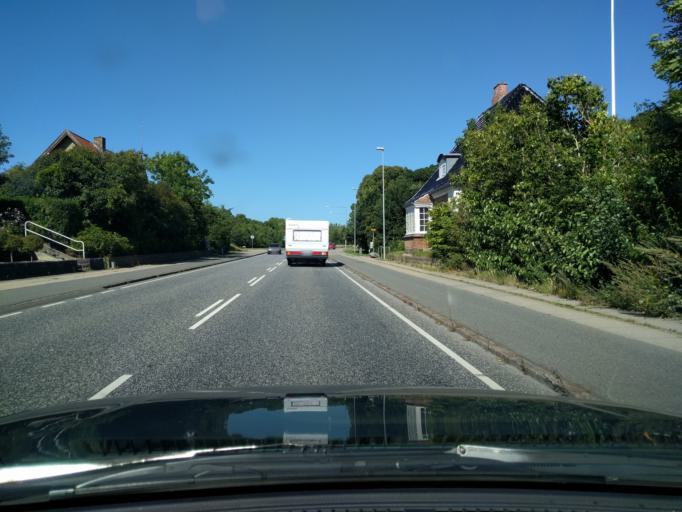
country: DK
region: Zealand
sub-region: Slagelse Kommune
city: Korsor
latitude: 55.3439
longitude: 11.1406
